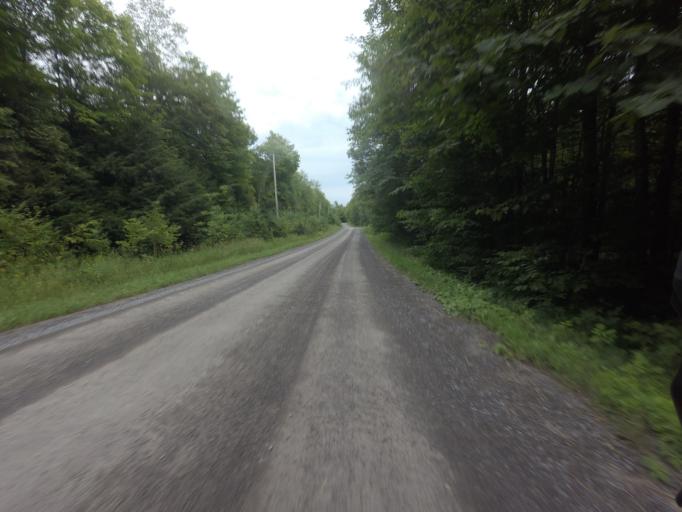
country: CA
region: Ontario
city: Carleton Place
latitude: 45.1514
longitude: -76.2576
